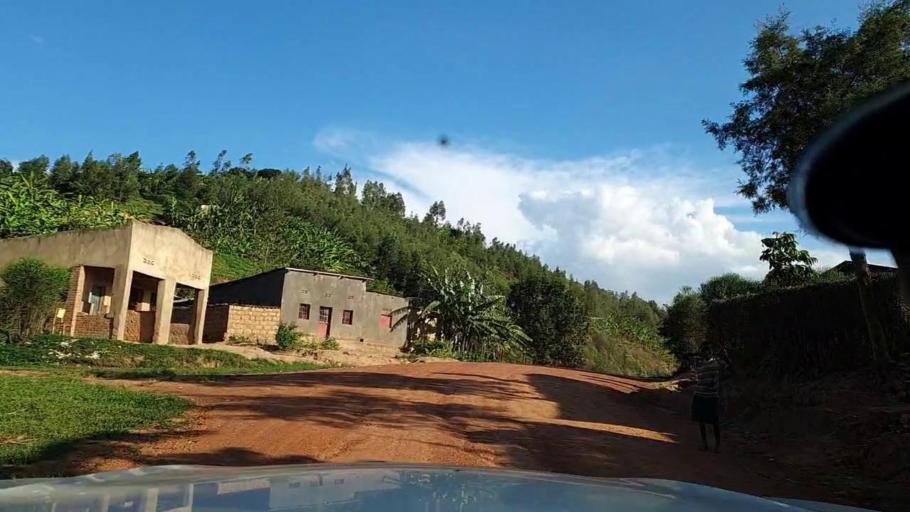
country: RW
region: Kigali
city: Kigali
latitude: -1.8654
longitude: 29.9312
